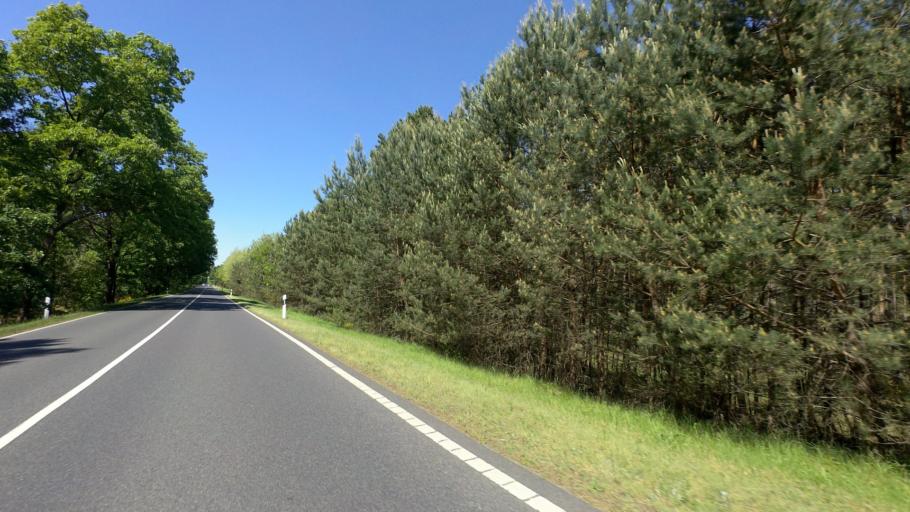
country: DE
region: Brandenburg
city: Lieberose
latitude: 51.9557
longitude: 14.3296
